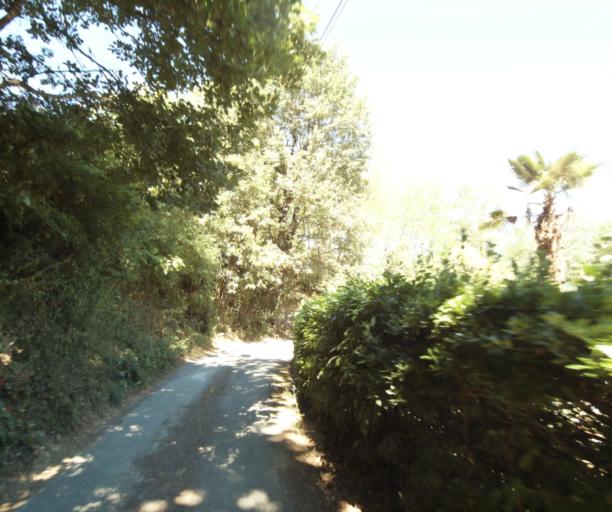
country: FR
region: Midi-Pyrenees
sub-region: Departement de la Haute-Garonne
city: Castanet-Tolosan
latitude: 43.5087
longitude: 1.4924
